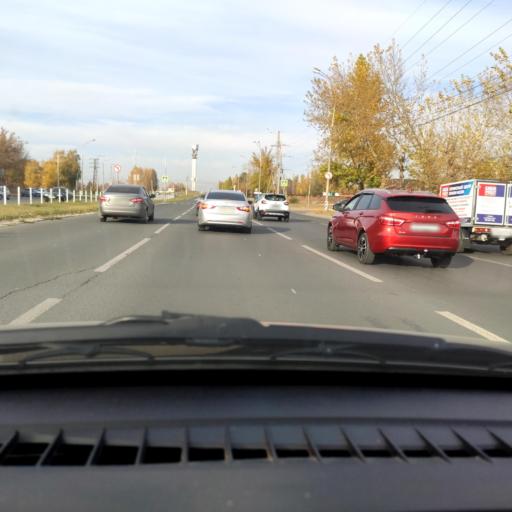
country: RU
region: Samara
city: Tol'yatti
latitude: 53.5504
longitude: 49.2870
